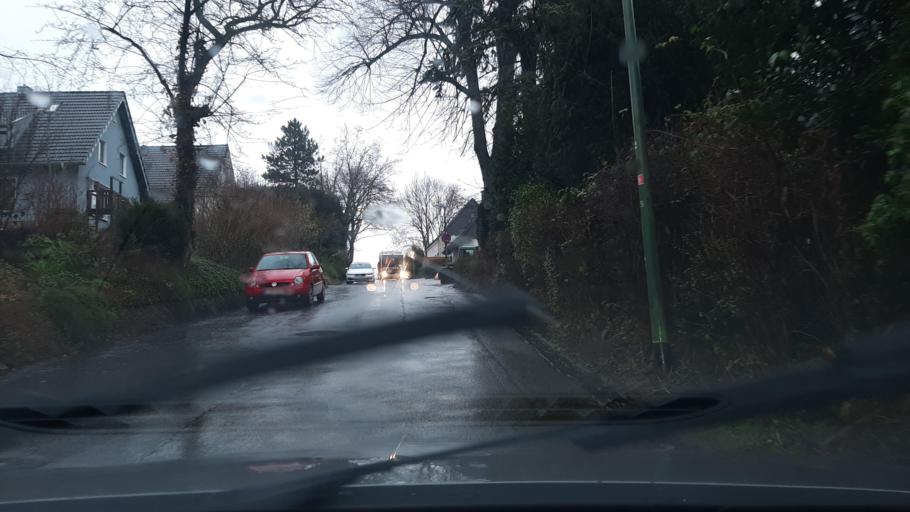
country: DE
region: North Rhine-Westphalia
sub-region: Regierungsbezirk Dusseldorf
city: Essen
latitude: 51.4377
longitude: 6.9734
